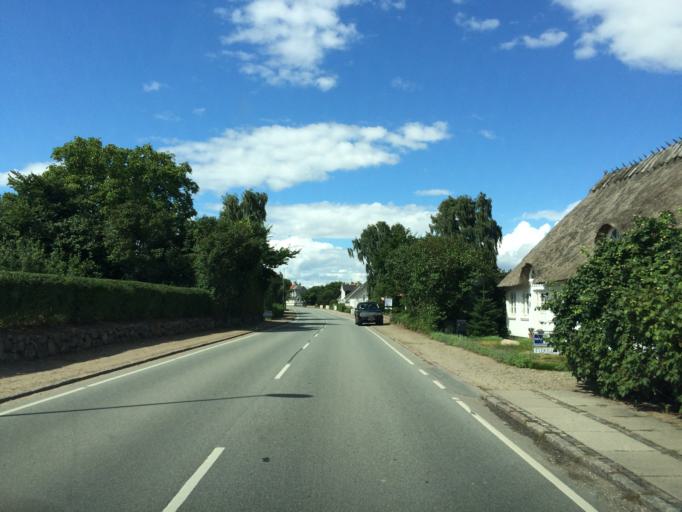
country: DK
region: South Denmark
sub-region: Faaborg-Midtfyn Kommune
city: Faaborg
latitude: 55.1345
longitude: 10.2009
